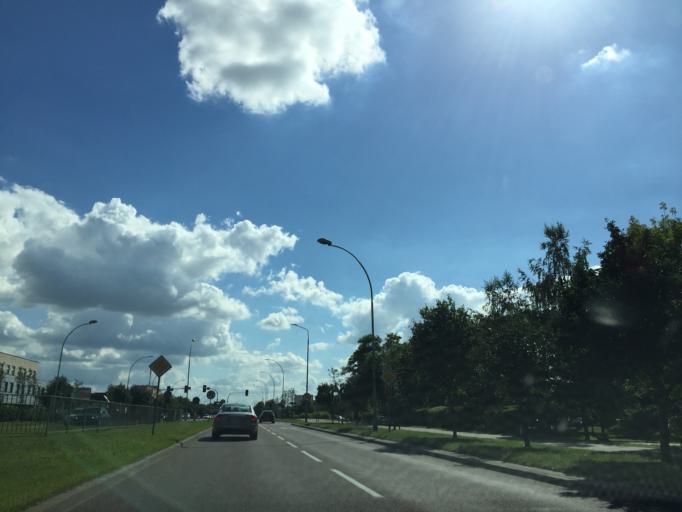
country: PL
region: Podlasie
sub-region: Suwalki
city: Suwalki
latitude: 54.1216
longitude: 22.9407
